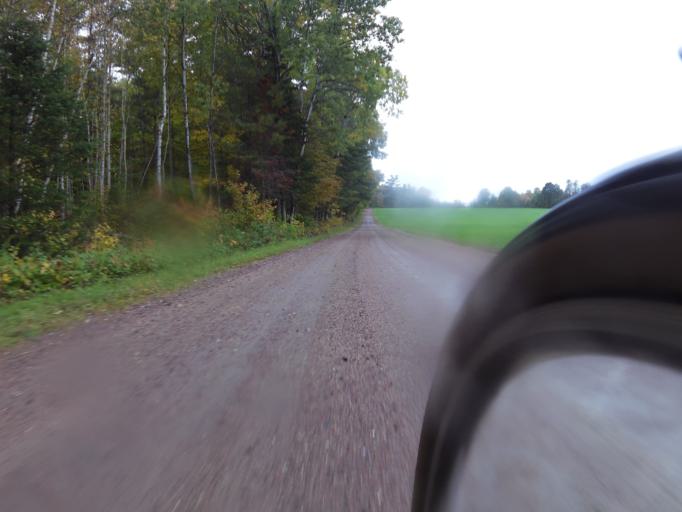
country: CA
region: Quebec
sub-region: Outaouais
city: Shawville
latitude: 45.6788
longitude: -76.5445
